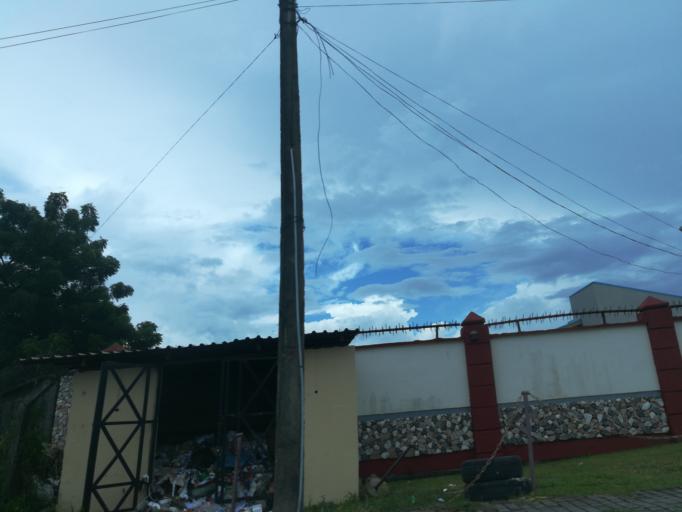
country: NG
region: Lagos
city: Ikoyi
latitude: 6.4427
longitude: 3.4713
